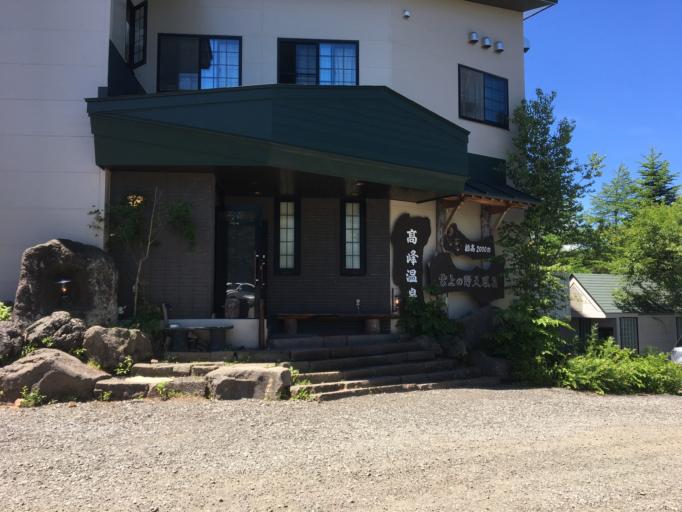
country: JP
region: Nagano
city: Komoro
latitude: 36.4102
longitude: 138.4596
